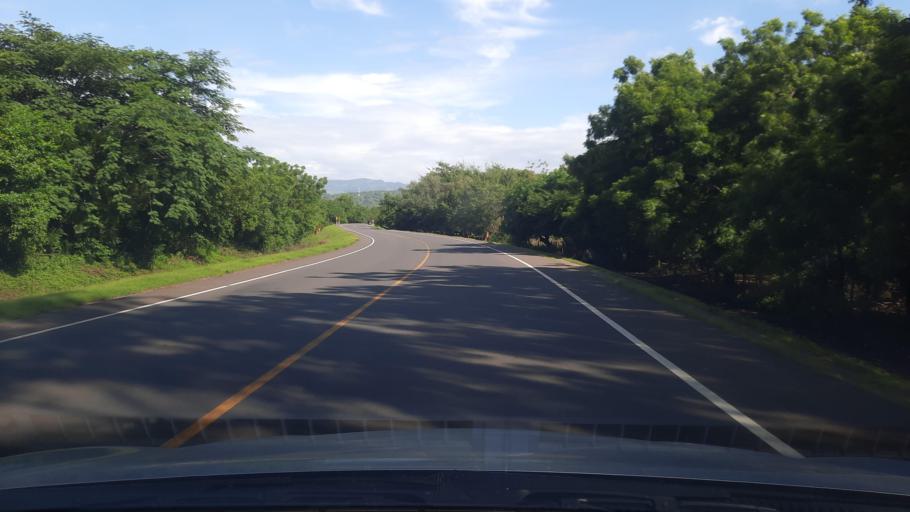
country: NI
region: Leon
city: Telica
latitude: 12.7205
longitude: -86.8773
